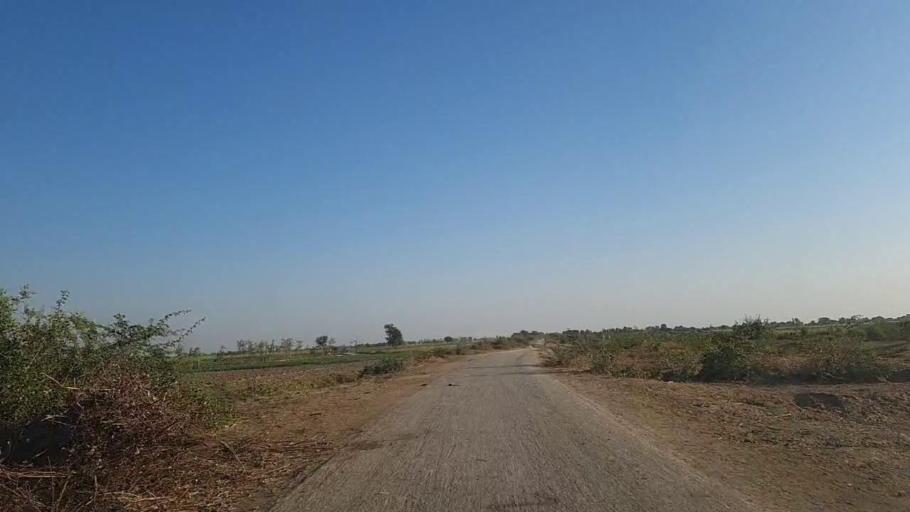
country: PK
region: Sindh
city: Naukot
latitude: 24.9866
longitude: 69.4042
